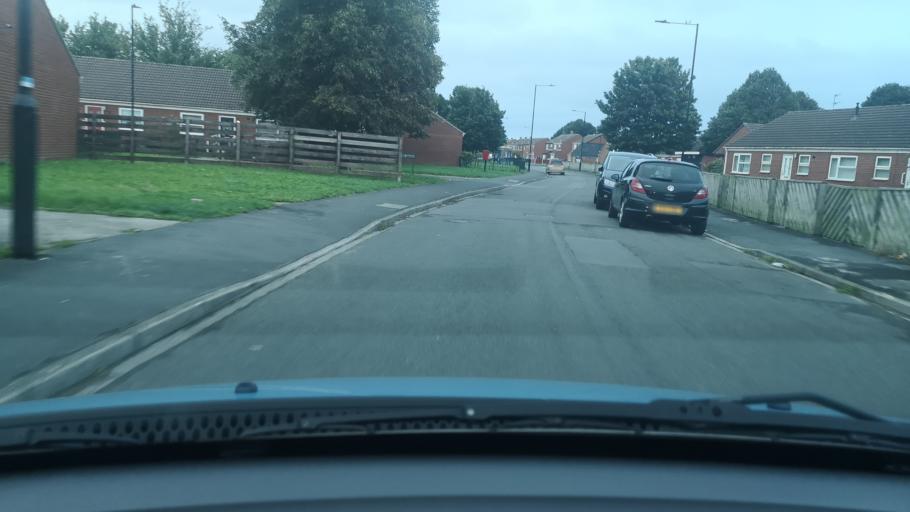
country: GB
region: England
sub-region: Doncaster
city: Askern
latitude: 53.6145
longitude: -1.1410
